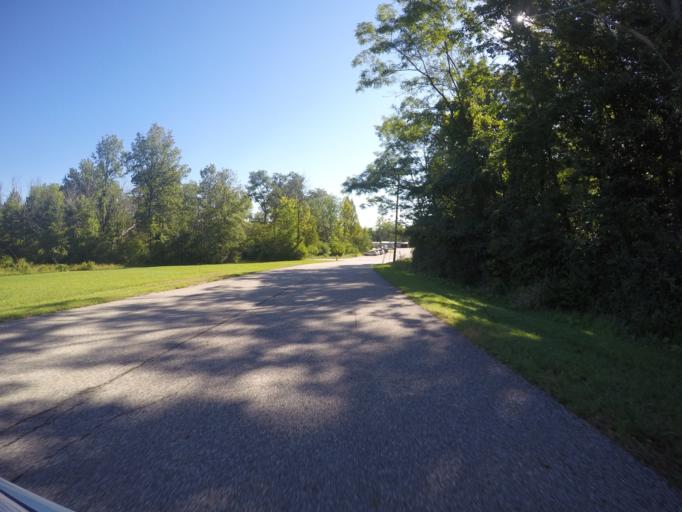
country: US
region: Ohio
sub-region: Cuyahoga County
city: Brecksville
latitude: 41.3092
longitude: -81.6249
